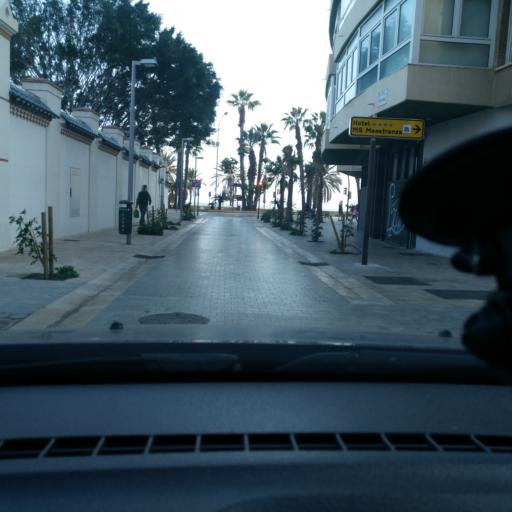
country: ES
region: Andalusia
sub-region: Provincia de Malaga
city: Malaga
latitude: 36.7196
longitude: -4.4079
